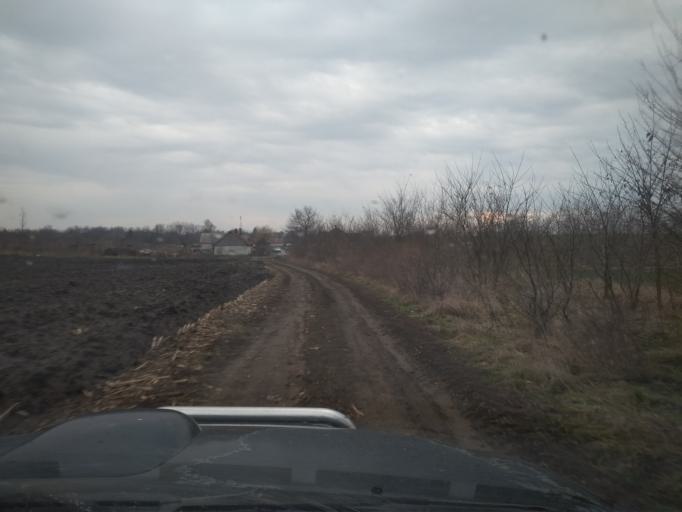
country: HU
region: Szabolcs-Szatmar-Bereg
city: Nagycserkesz
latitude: 47.9764
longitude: 21.5537
